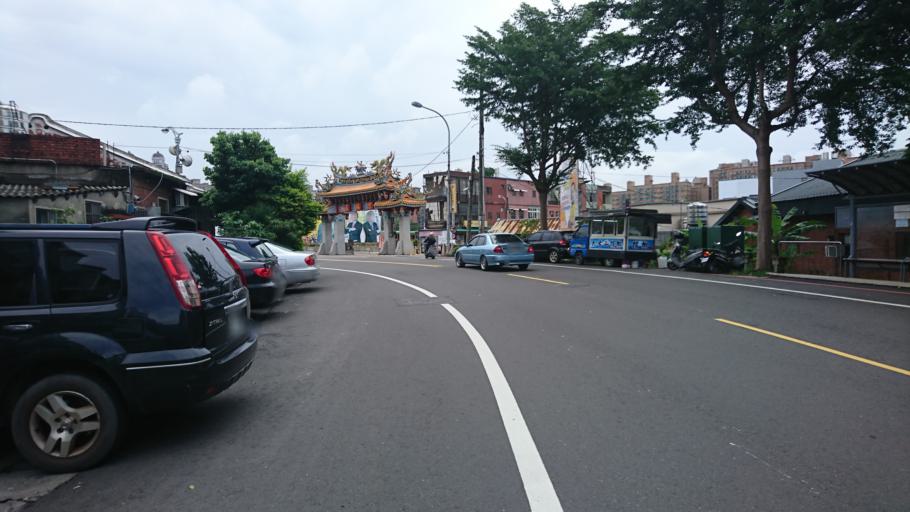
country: TW
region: Taiwan
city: Taoyuan City
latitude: 25.0540
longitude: 121.2947
